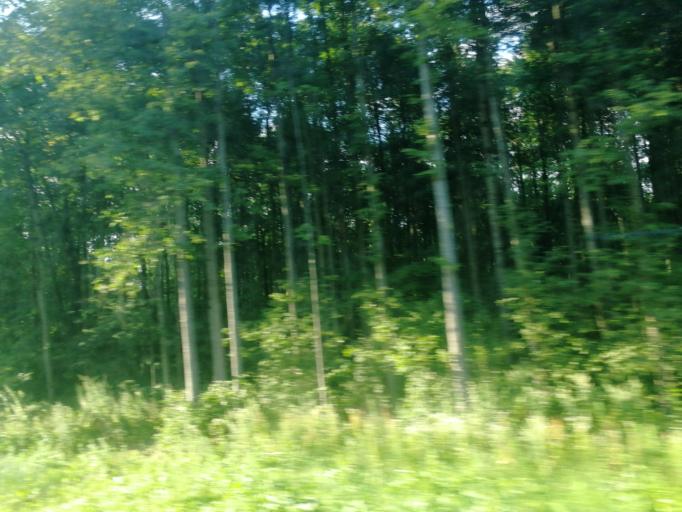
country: RU
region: Kaluga
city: Kaluga
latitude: 54.4493
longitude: 36.3045
